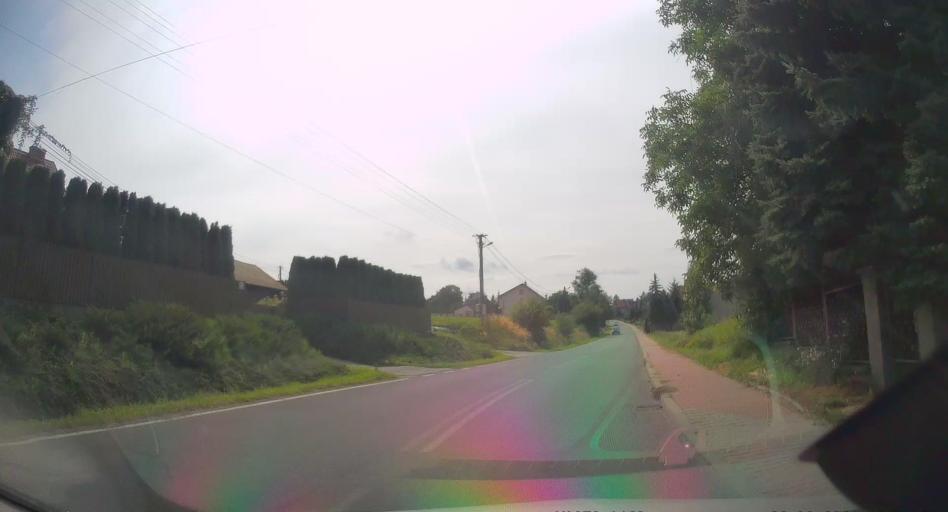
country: PL
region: Lesser Poland Voivodeship
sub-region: Powiat myslenicki
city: Borzeta
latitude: 49.8895
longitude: 20.0006
